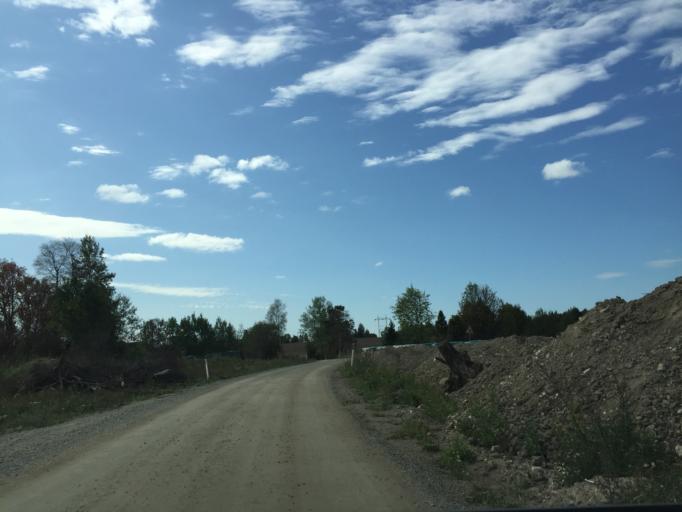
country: NO
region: Ostfold
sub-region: Hobol
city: Elvestad
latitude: 59.6365
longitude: 10.8873
